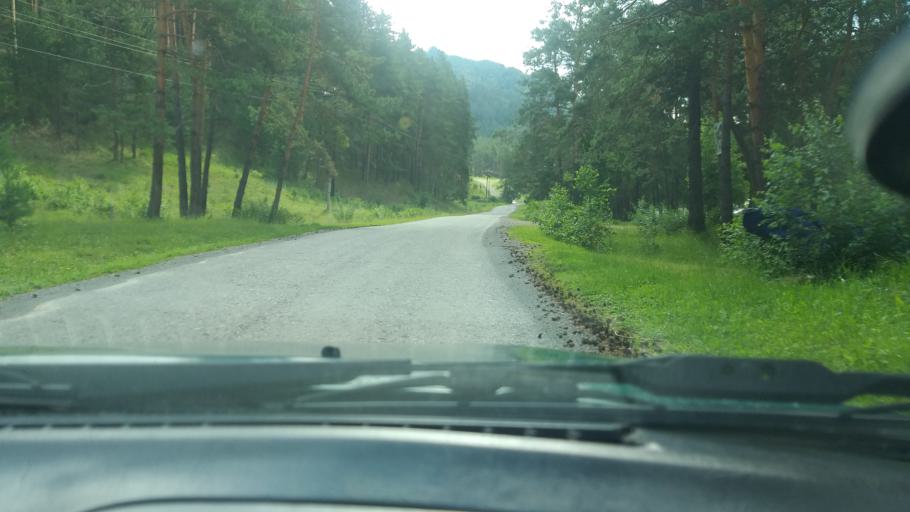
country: RU
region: Altay
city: Chemal
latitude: 51.3919
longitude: 86.0445
